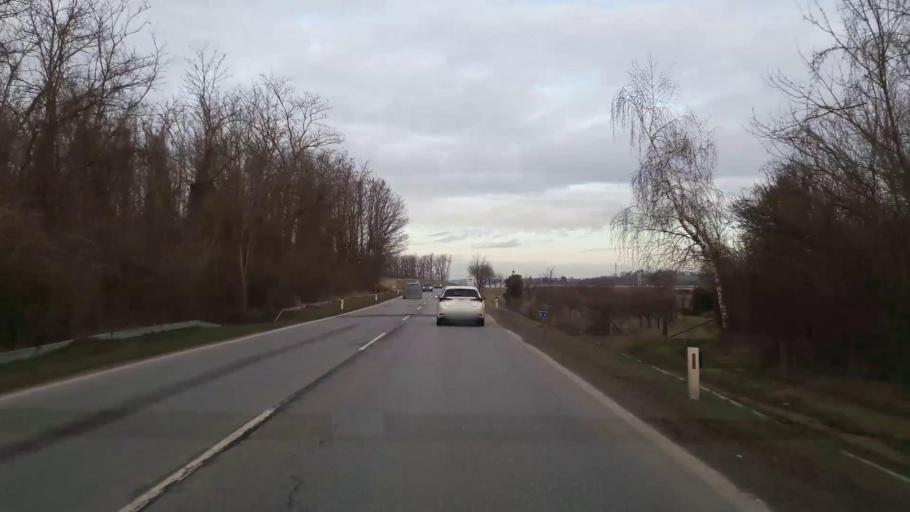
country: AT
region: Lower Austria
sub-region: Politischer Bezirk Mistelbach
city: Mistelbach
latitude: 48.5480
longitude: 16.5871
